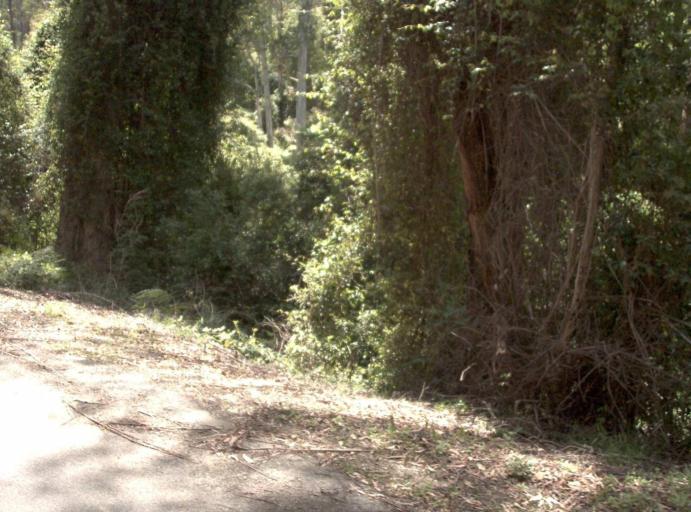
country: AU
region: New South Wales
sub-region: Bombala
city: Bombala
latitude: -37.4837
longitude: 148.9286
